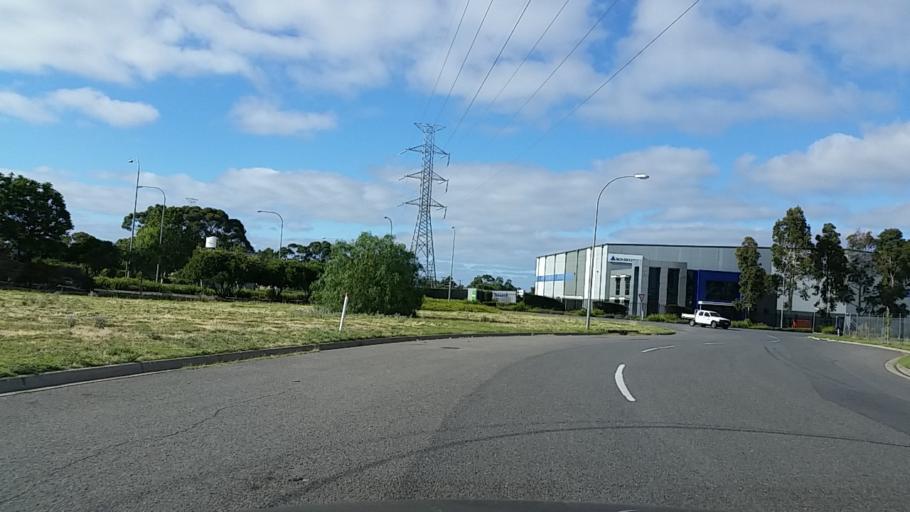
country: AU
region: South Australia
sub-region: Port Adelaide Enfield
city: Enfield
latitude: -34.8329
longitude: 138.6103
